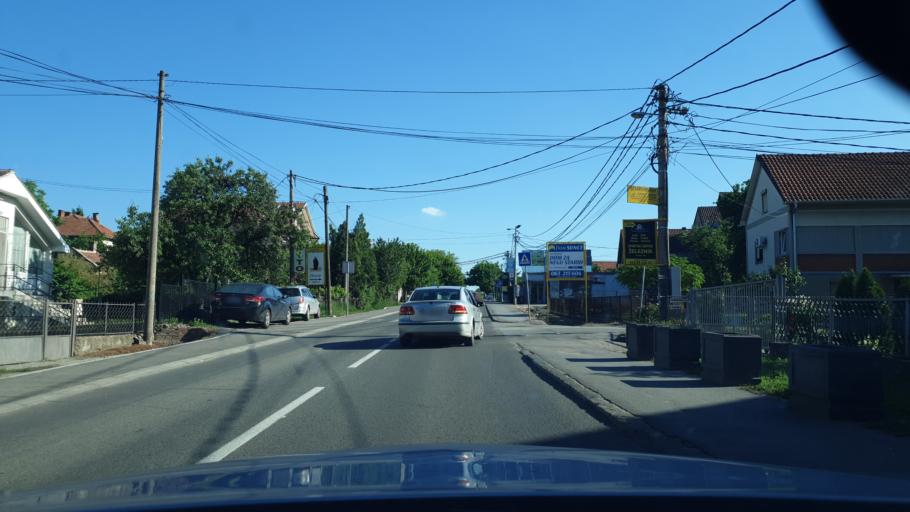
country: RS
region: Central Serbia
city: Sremcica
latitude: 44.7153
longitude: 20.3683
